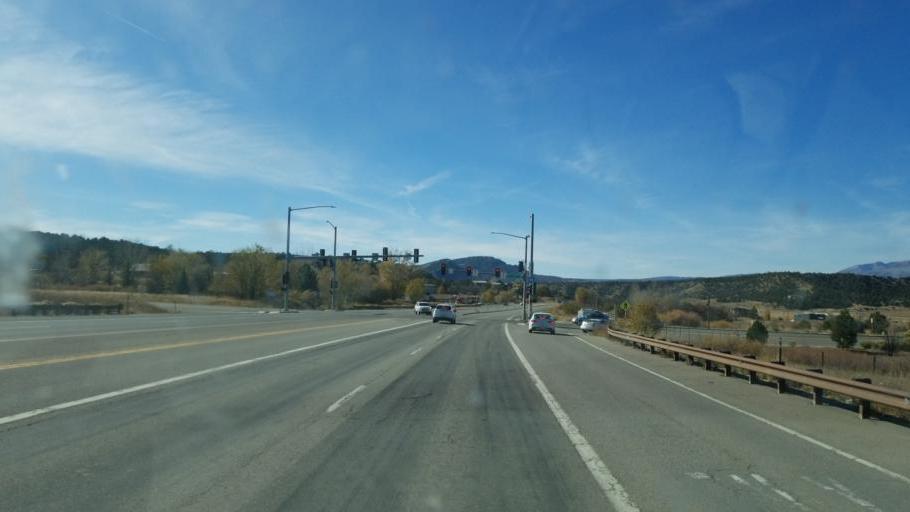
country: US
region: Colorado
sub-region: La Plata County
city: Durango
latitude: 37.2272
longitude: -107.8191
